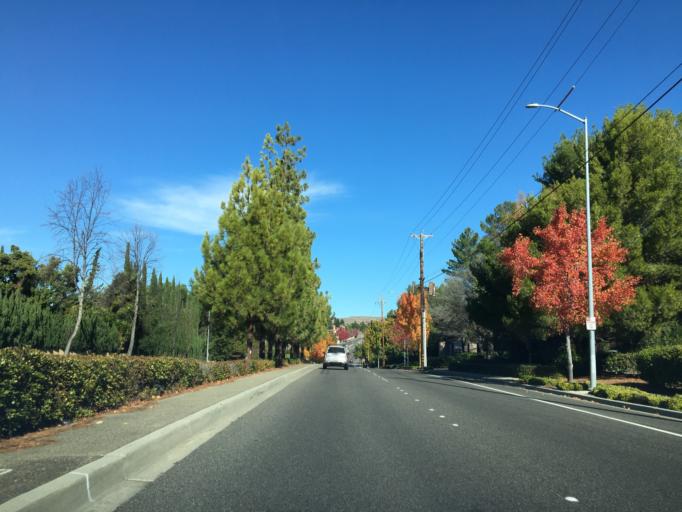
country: US
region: California
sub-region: Alameda County
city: Fremont
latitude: 37.5106
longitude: -121.9198
